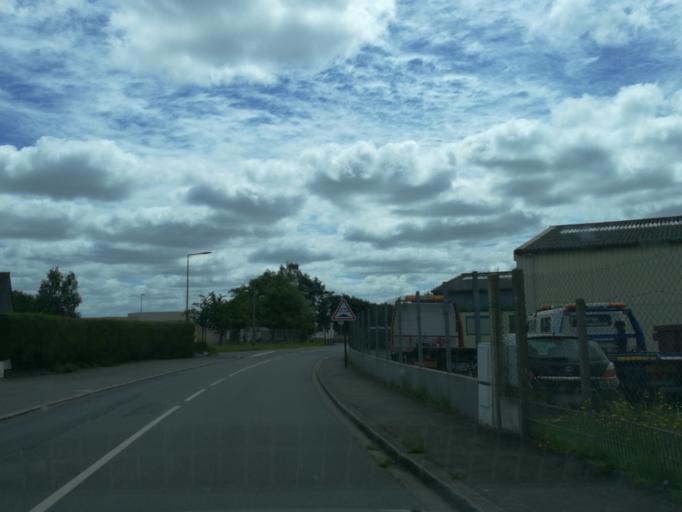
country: FR
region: Brittany
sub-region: Departement d'Ille-et-Vilaine
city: Bedee
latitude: 48.1814
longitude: -1.9350
